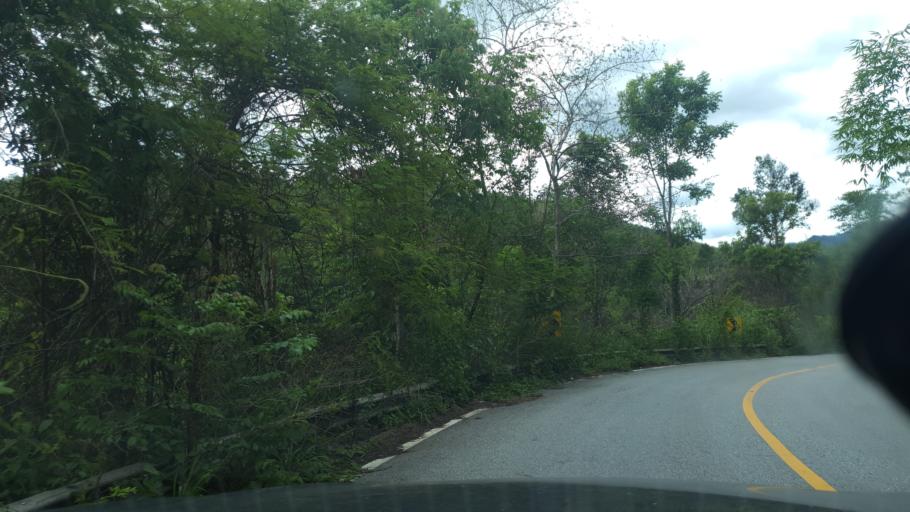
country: TH
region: Lampang
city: Thoen
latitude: 17.6790
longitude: 99.0675
